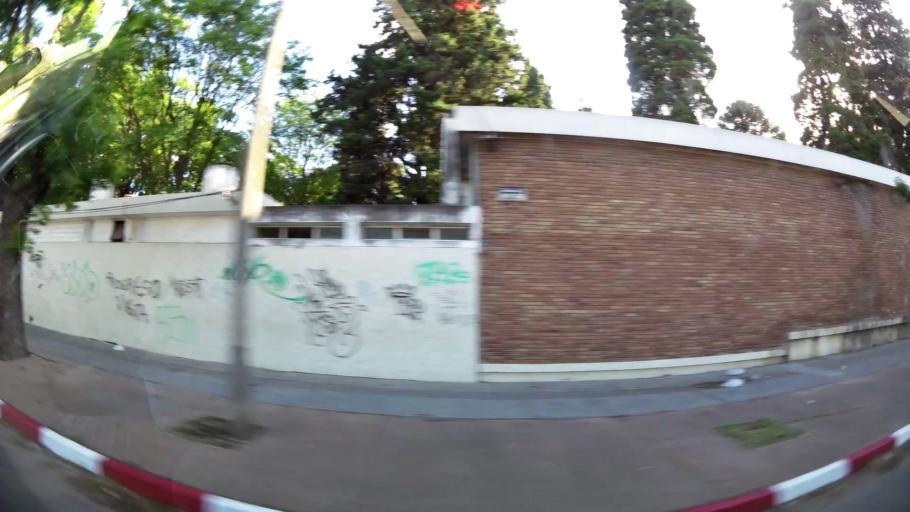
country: UY
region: Montevideo
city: Montevideo
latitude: -34.8582
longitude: -56.2285
